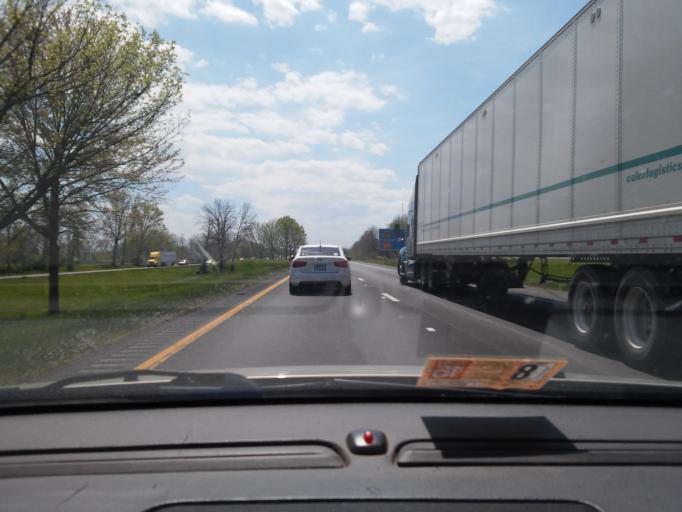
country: US
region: West Virginia
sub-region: Berkeley County
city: Martinsburg
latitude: 39.4249
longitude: -78.0025
